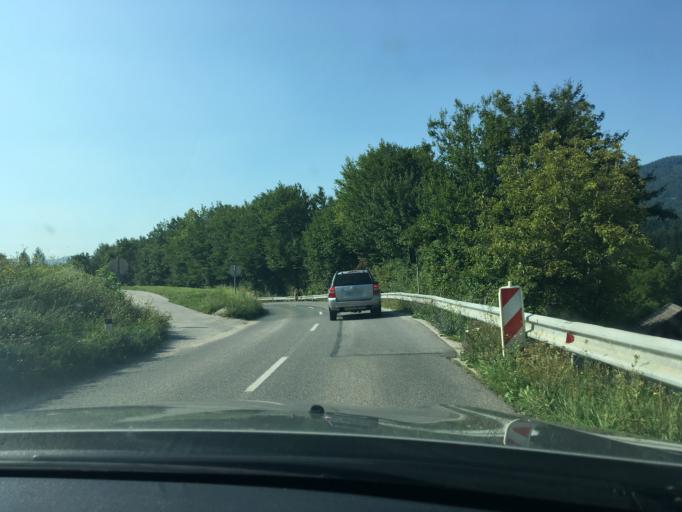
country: SI
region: Dolenjske Toplice
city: Dolenjske Toplice
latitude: 45.7676
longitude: 15.0532
